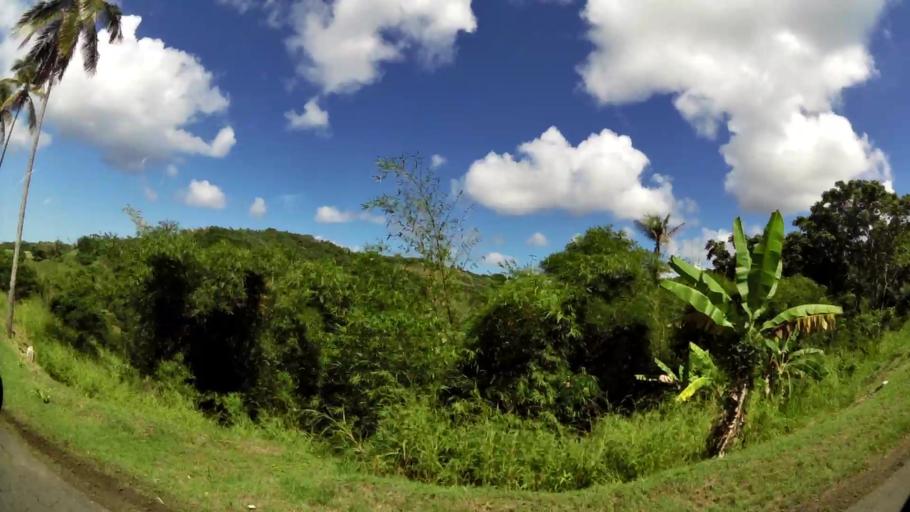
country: TT
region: Tobago
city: Scarborough
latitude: 11.1868
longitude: -60.7842
